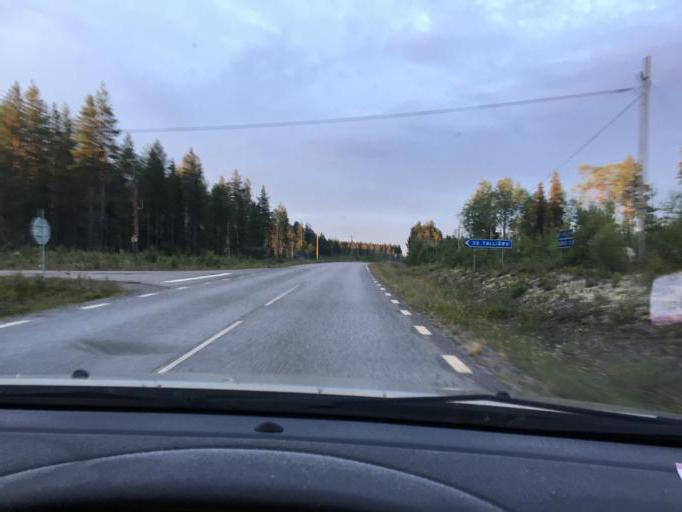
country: SE
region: Norrbotten
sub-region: Kalix Kommun
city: Toere
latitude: 66.0537
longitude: 22.5622
